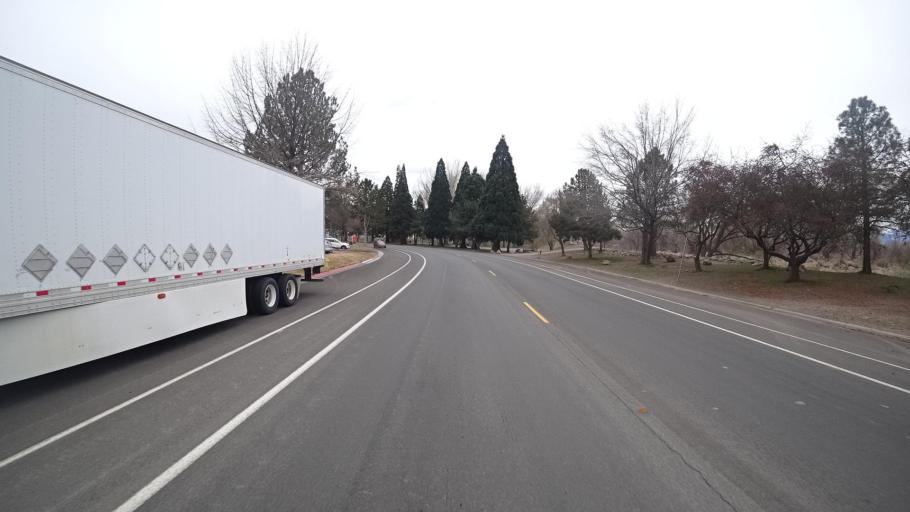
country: US
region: Nevada
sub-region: Washoe County
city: Sparks
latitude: 39.5137
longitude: -119.7333
